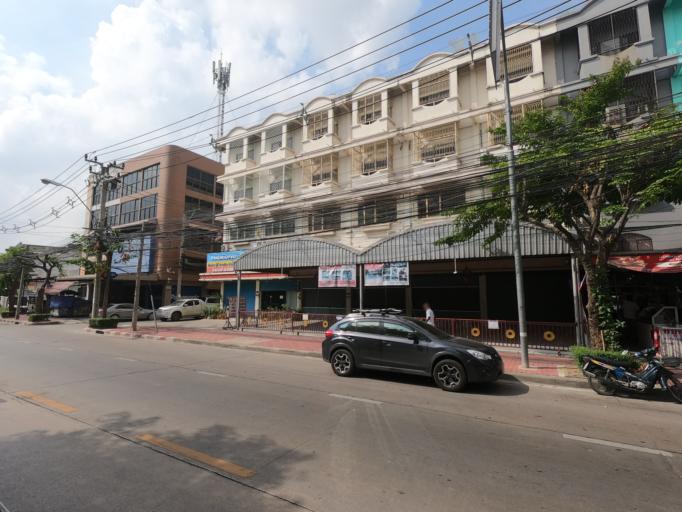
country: TH
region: Bangkok
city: Lat Phrao
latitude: 13.8195
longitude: 100.6094
